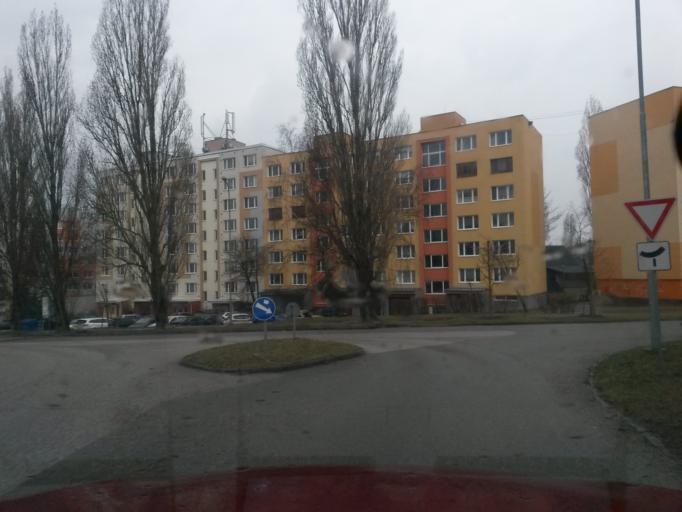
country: SK
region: Kosicky
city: Kosice
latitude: 48.7350
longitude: 21.2915
